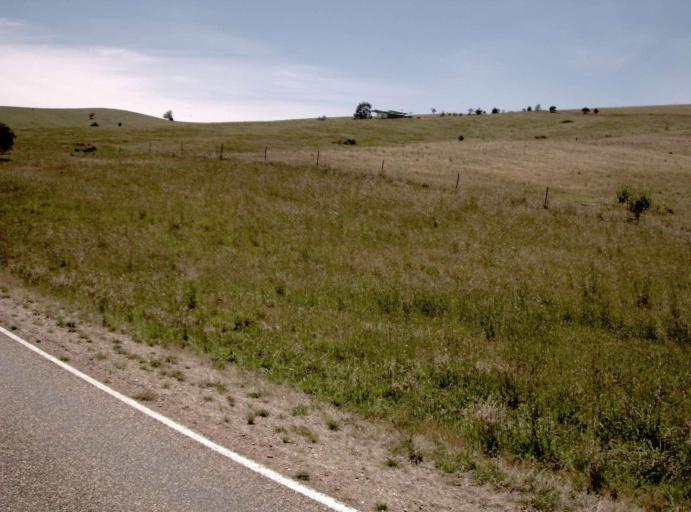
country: AU
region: Victoria
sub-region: Alpine
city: Mount Beauty
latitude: -36.9894
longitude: 147.6939
